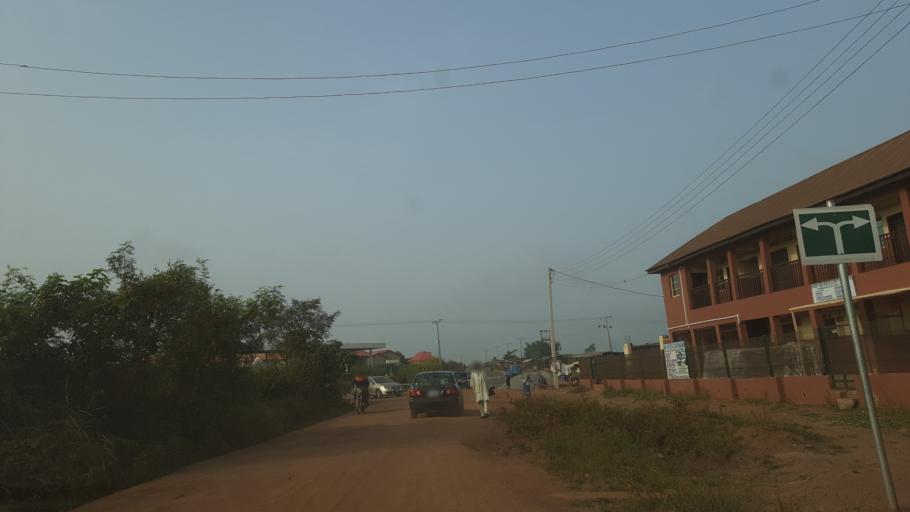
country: NG
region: Osun
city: Ilobu
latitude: 7.7918
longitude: 4.4997
